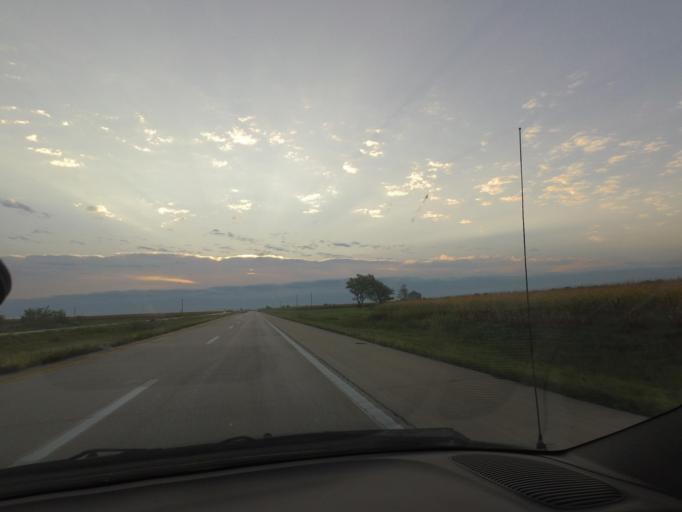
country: US
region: Missouri
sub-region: Macon County
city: Macon
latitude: 39.7498
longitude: -92.3159
